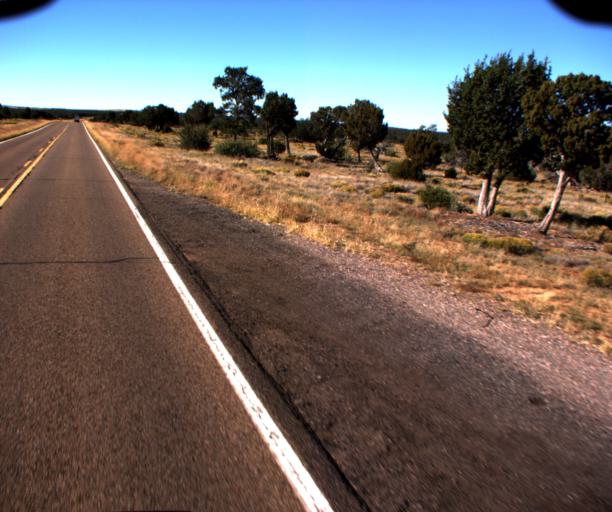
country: US
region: Arizona
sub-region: Navajo County
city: Heber-Overgaard
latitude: 34.4960
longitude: -110.4552
